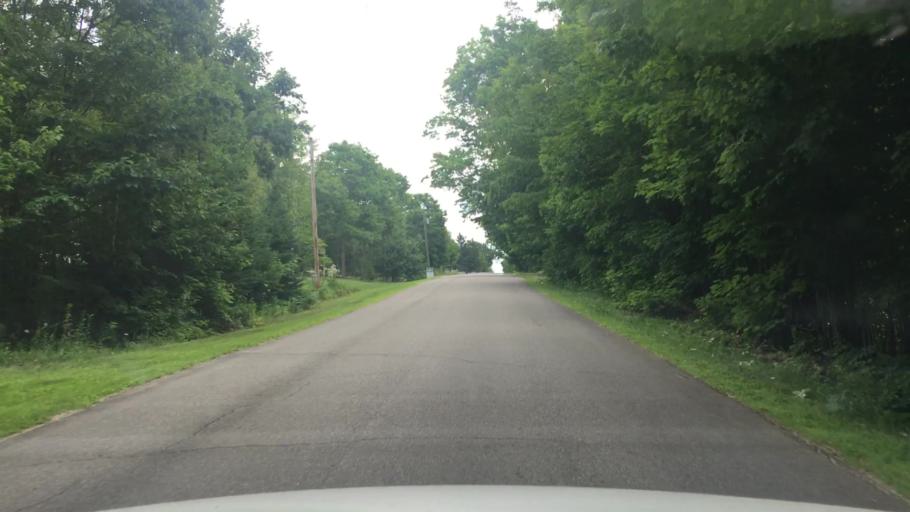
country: US
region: Maine
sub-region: Kennebec County
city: Albion
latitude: 44.4797
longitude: -69.3712
